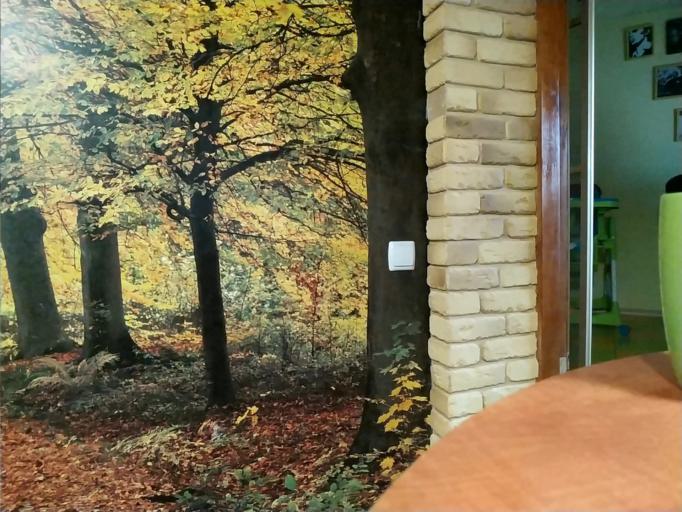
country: RU
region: Tverskaya
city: Staraya Toropa
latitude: 56.3510
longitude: 31.8135
